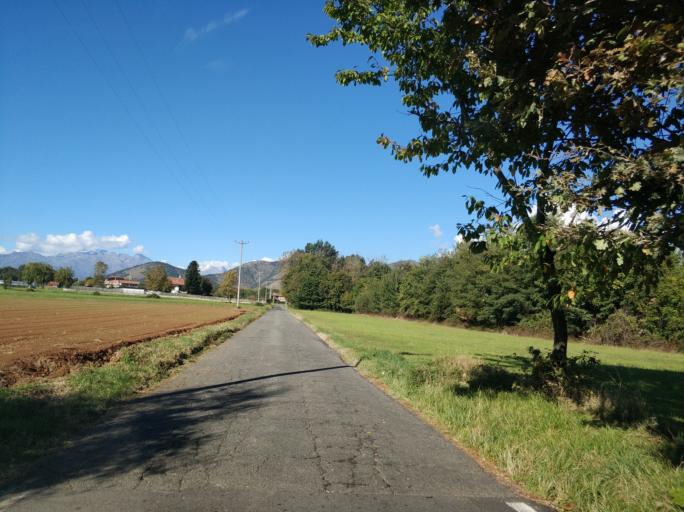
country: IT
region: Piedmont
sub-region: Provincia di Torino
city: Rocca Canavese
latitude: 45.2816
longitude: 7.5791
